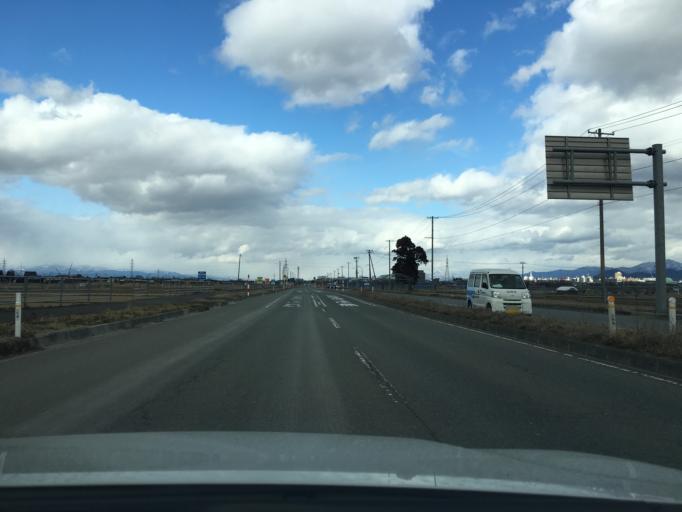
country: JP
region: Yamagata
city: Kaminoyama
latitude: 38.2121
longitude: 140.3005
